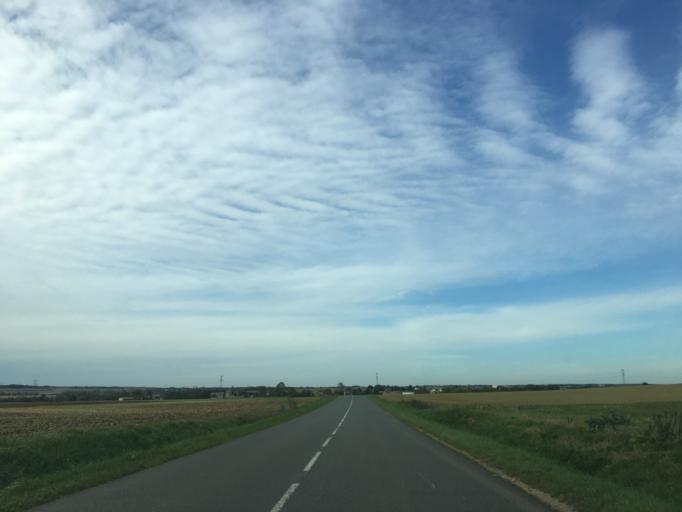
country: FR
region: Poitou-Charentes
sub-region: Departement de la Charente-Maritime
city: Aulnay
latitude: 46.0699
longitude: -0.4449
